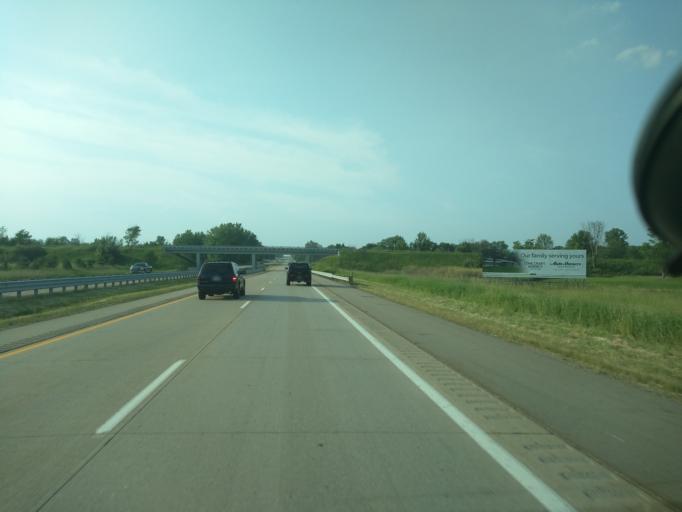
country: US
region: Michigan
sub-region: Ingham County
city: Leslie
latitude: 42.3478
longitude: -84.4288
